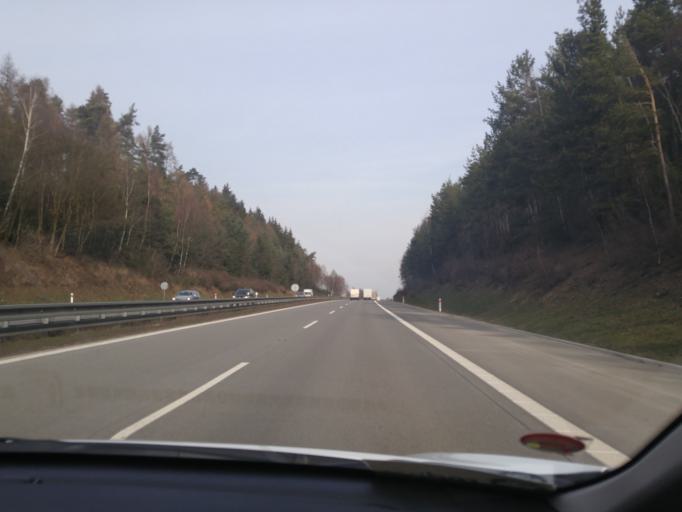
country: CZ
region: Central Bohemia
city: Cechtice
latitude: 49.6288
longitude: 15.1306
